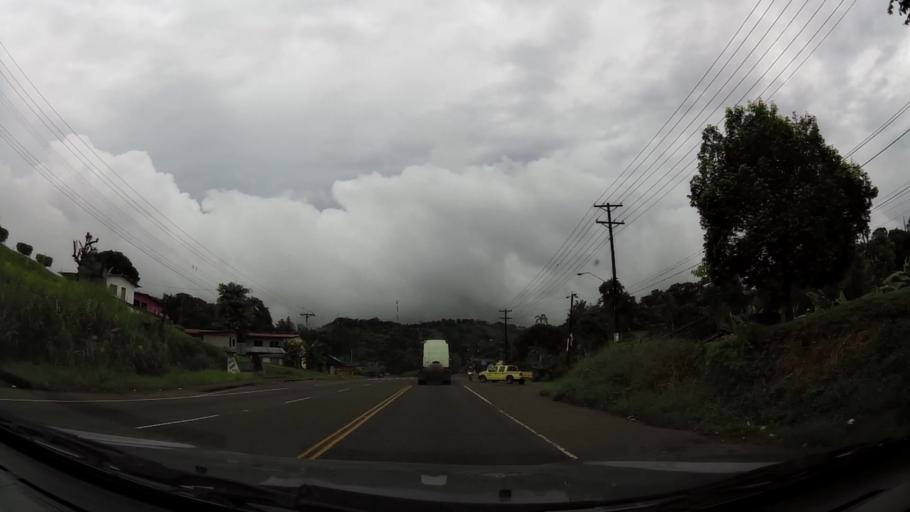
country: PA
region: Colon
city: Nuevo Vigia
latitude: 9.2354
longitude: -79.6313
